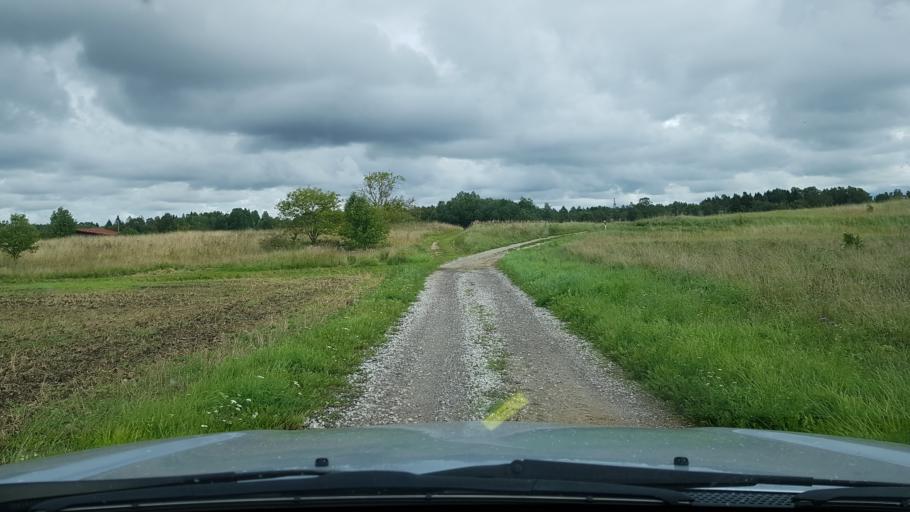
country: EE
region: Harju
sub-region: Rae vald
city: Vaida
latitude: 59.3493
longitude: 24.9859
